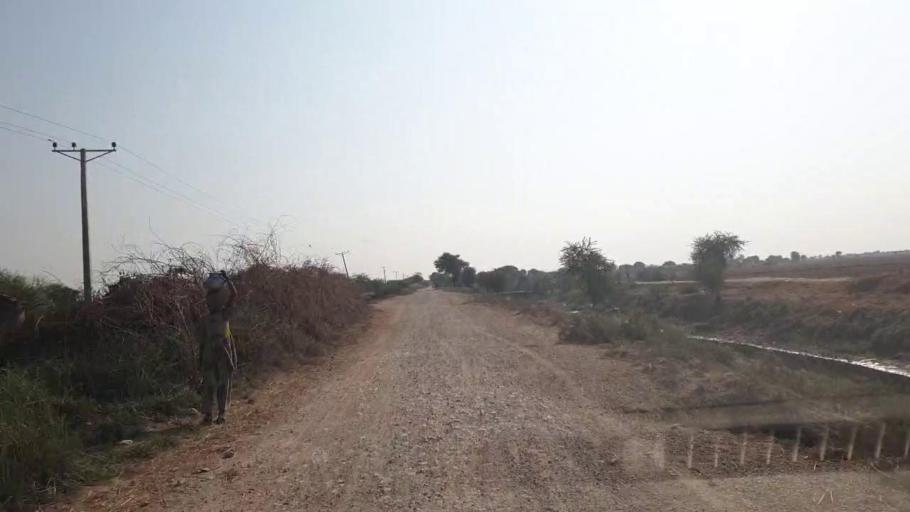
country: PK
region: Sindh
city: Kario
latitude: 24.9050
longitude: 68.6487
